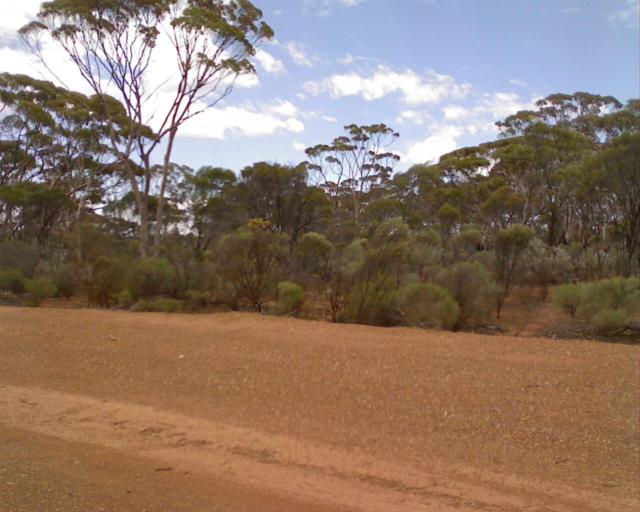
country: AU
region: Western Australia
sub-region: Kalgoorlie/Boulder
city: Stoneville
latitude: -31.1096
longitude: 121.6180
